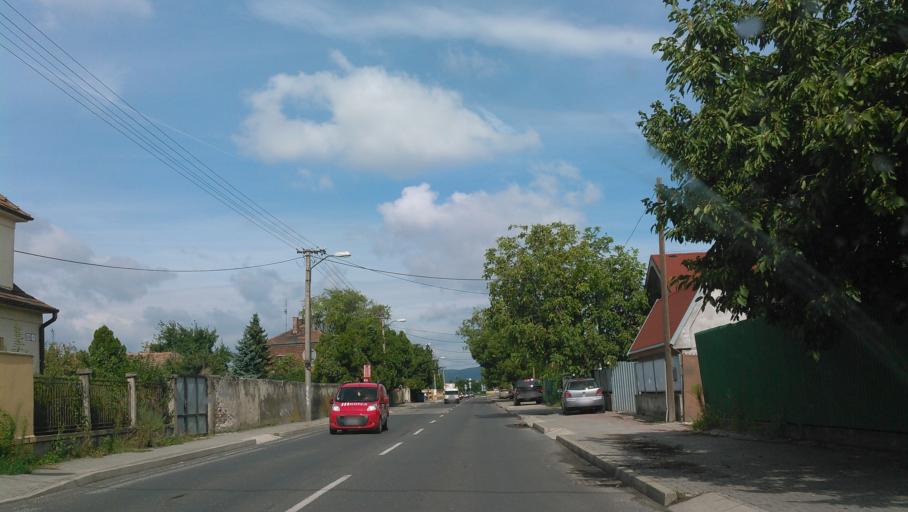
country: SK
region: Bratislavsky
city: Bratislava
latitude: 48.1532
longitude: 17.1973
